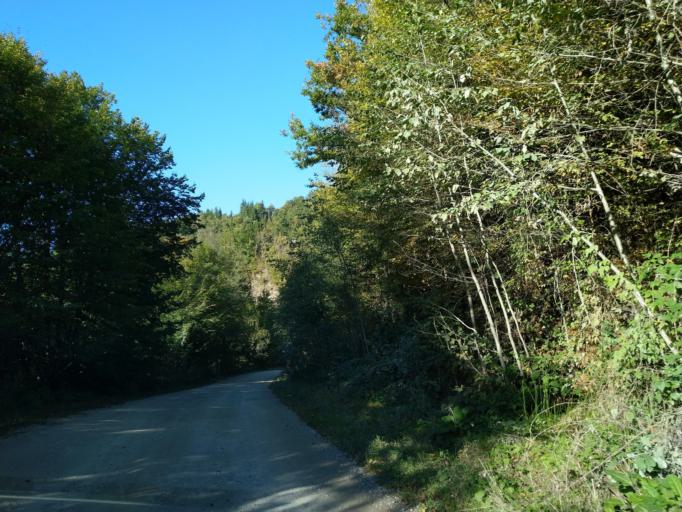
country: RS
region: Central Serbia
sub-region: Moravicki Okrug
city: Ivanjica
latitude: 43.4783
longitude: 20.2392
